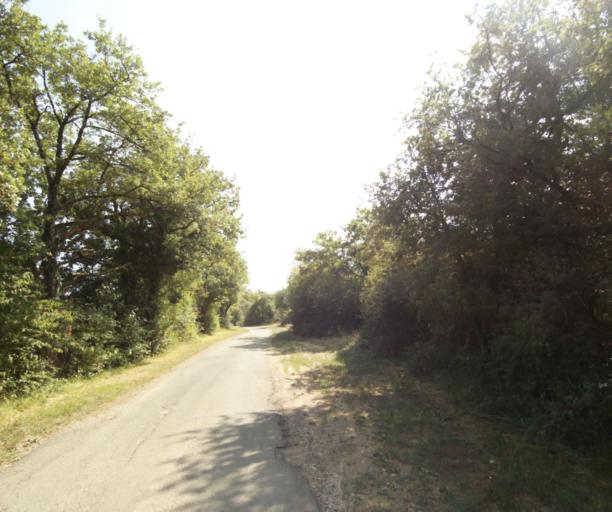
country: FR
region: Bourgogne
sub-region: Departement de Saone-et-Loire
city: Tournus
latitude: 46.5528
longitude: 4.8732
